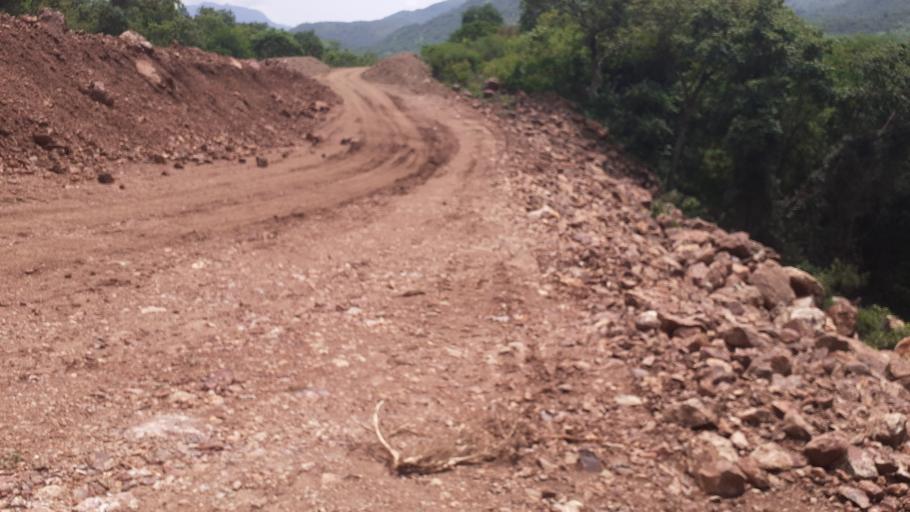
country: ET
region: Southern Nations, Nationalities, and People's Region
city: Areka
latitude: 7.6111
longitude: 37.5234
